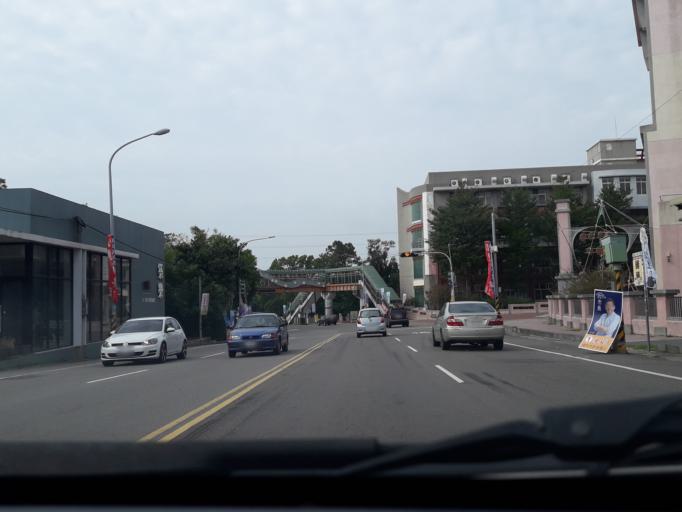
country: TW
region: Taiwan
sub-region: Hsinchu
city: Hsinchu
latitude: 24.6853
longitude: 120.9362
